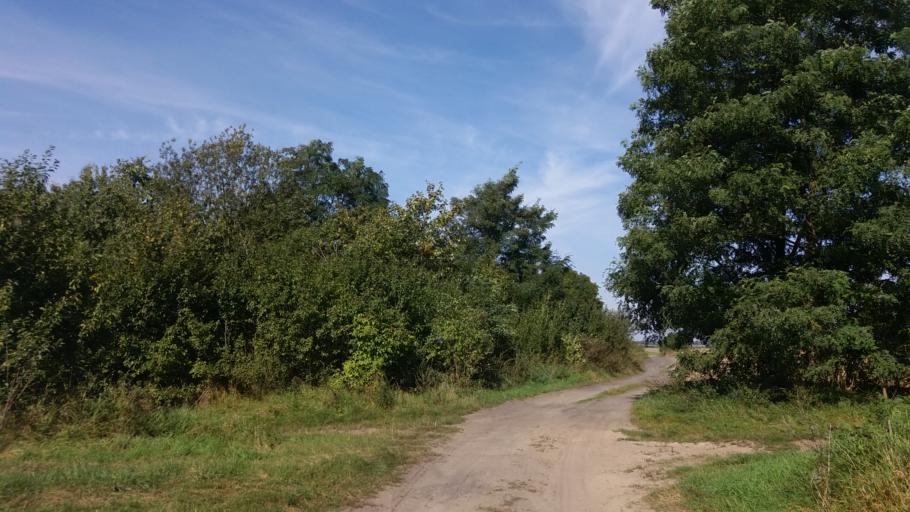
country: PL
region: West Pomeranian Voivodeship
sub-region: Powiat choszczenski
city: Choszczno
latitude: 53.1207
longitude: 15.4121
